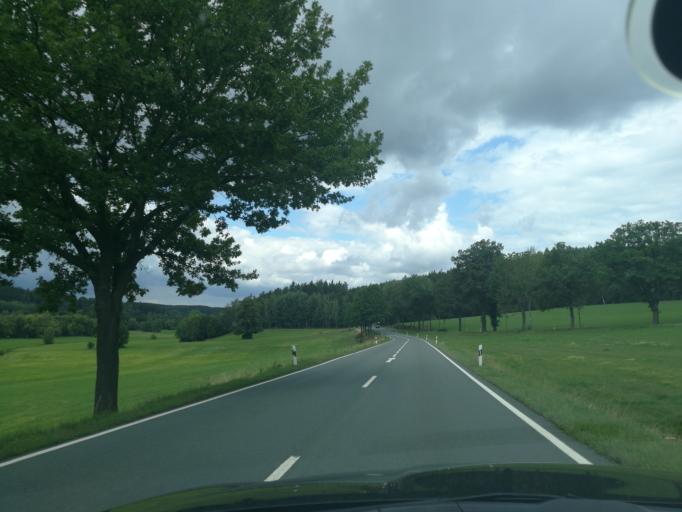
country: DE
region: Saxony
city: Eichigt
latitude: 50.3793
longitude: 12.2035
